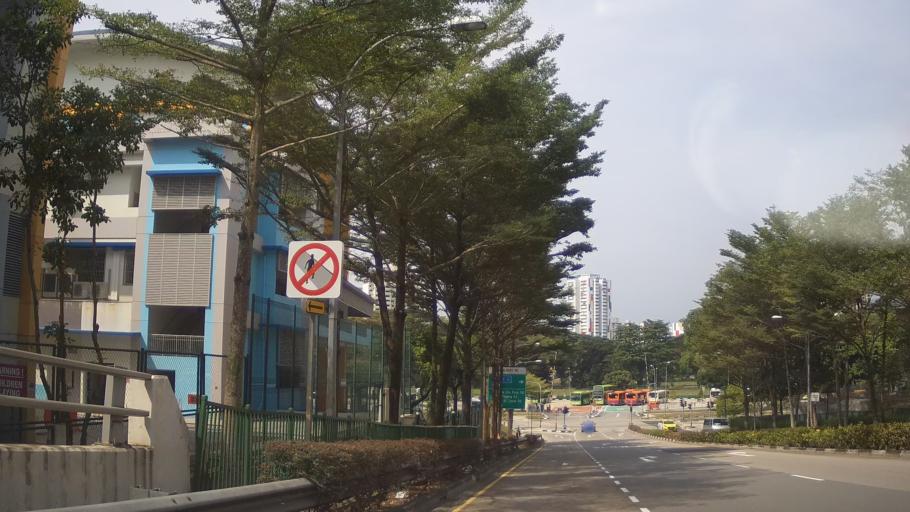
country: MY
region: Johor
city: Johor Bahru
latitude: 1.3842
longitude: 103.7599
